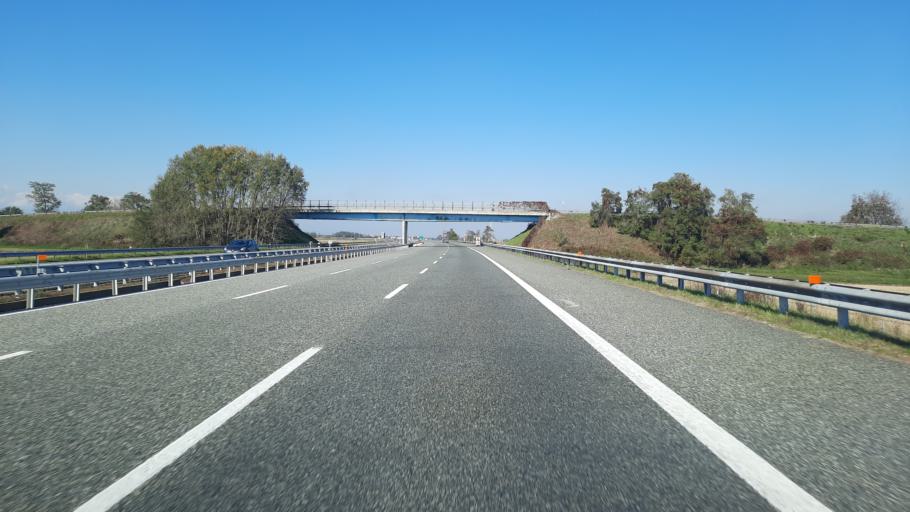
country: IT
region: Piedmont
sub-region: Provincia di Novara
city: Casalvolone
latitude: 45.3900
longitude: 8.4846
